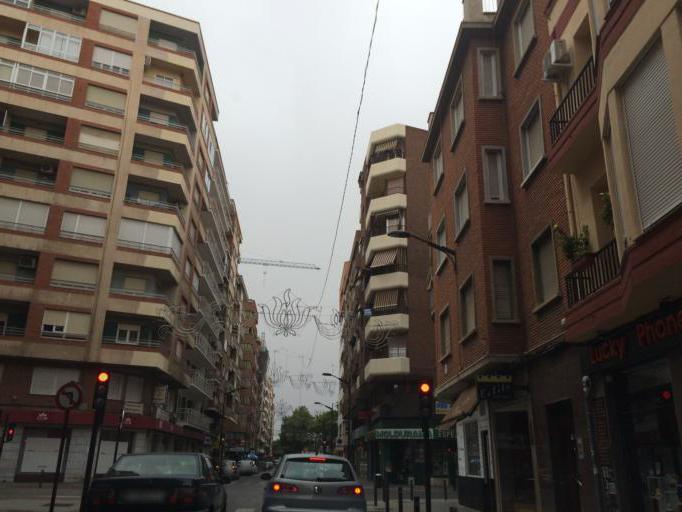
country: ES
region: Castille-La Mancha
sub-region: Provincia de Albacete
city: Albacete
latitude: 38.9958
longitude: -1.8596
